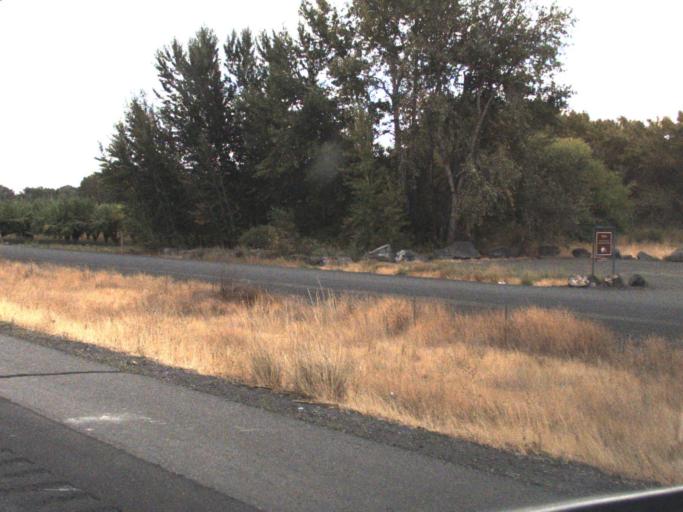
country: US
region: Washington
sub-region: Yakima County
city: Wapato
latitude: 46.4917
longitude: -120.4291
